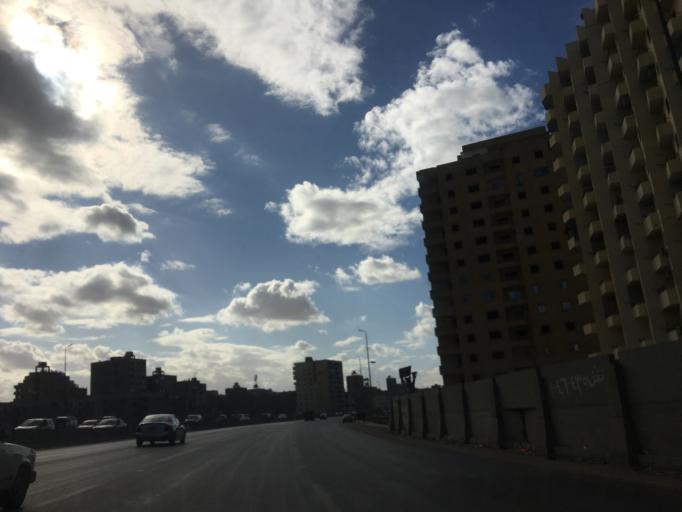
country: EG
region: Al Jizah
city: Al Jizah
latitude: 30.0147
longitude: 31.1637
